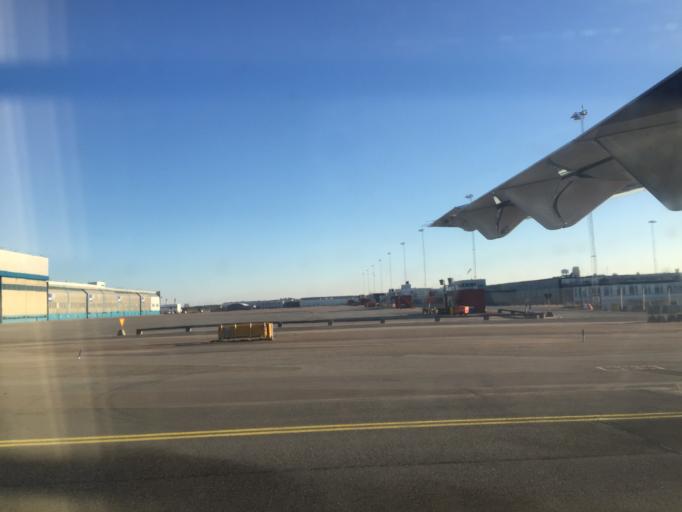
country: SE
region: Stockholm
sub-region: Sigtuna Kommun
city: Rosersberg
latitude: 59.6565
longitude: 17.9419
